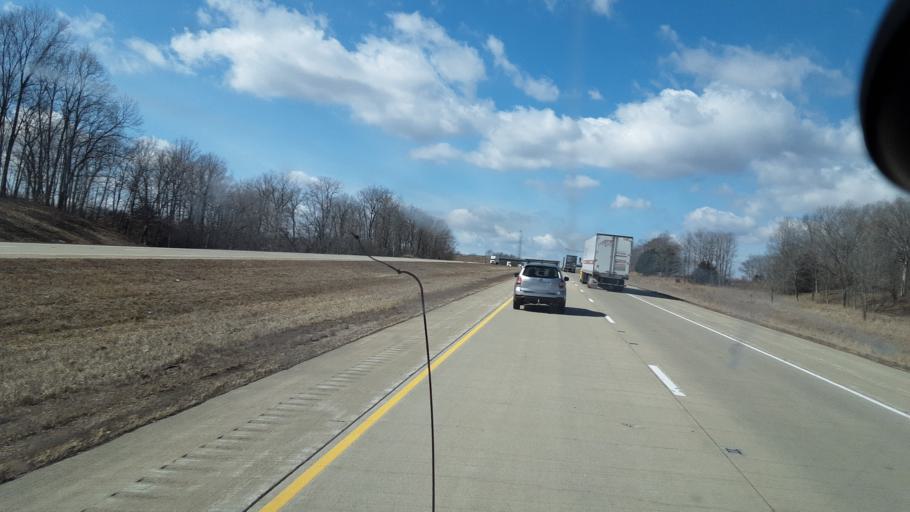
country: US
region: Illinois
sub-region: Clark County
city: Marshall
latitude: 39.4254
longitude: -87.5949
